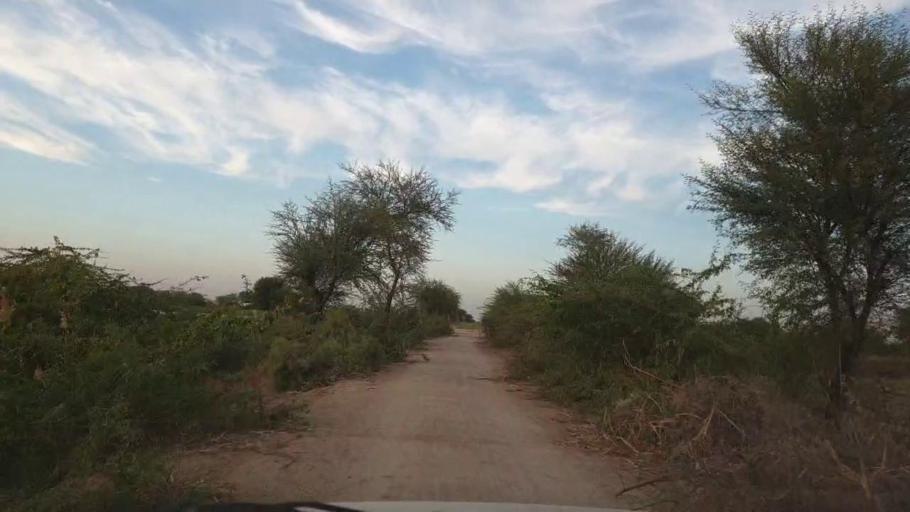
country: PK
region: Sindh
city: Pithoro
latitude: 25.6059
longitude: 69.2032
